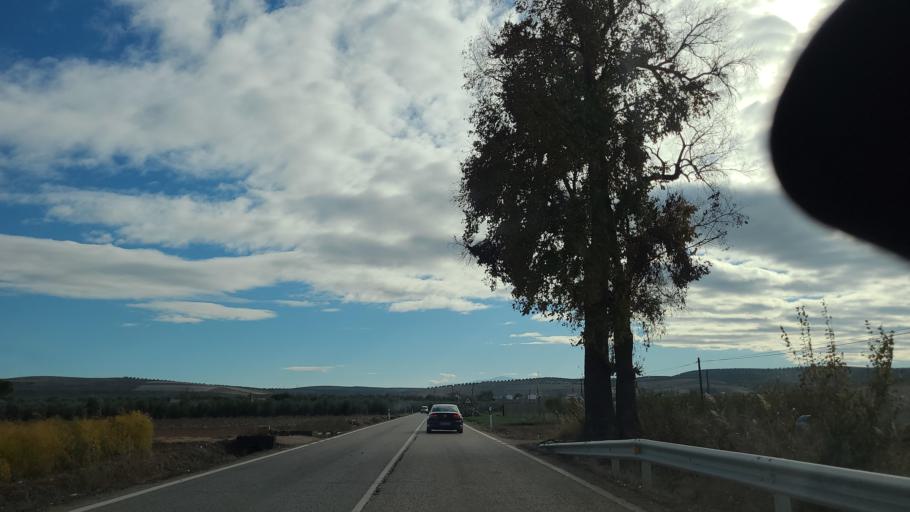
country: ES
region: Andalusia
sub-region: Provincia de Jaen
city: Villanueva de la Reina
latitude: 38.0160
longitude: -3.9133
